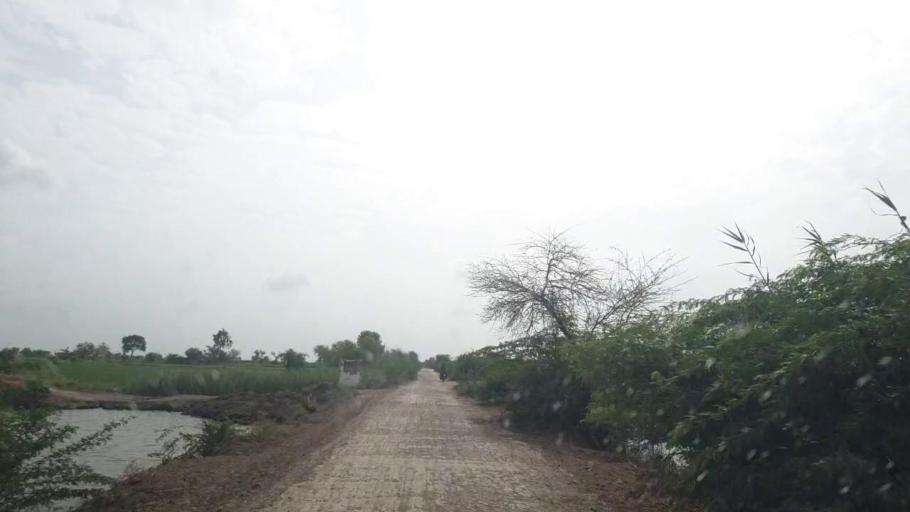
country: PK
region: Sindh
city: Tando Bago
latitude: 24.7922
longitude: 68.9808
